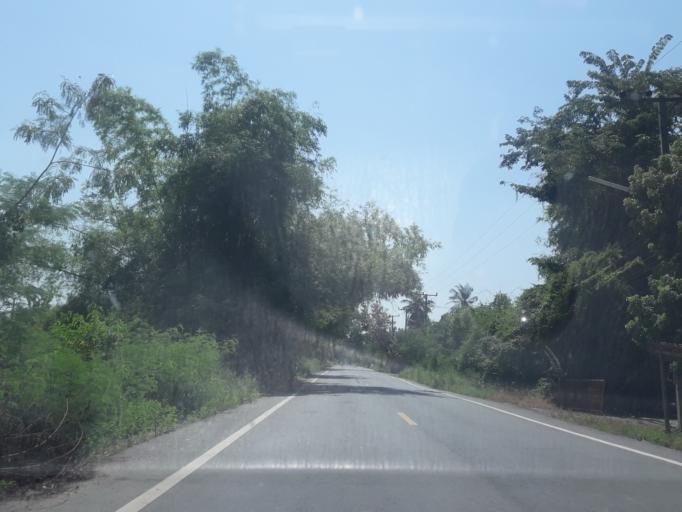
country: TH
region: Pathum Thani
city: Nong Suea
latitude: 14.1042
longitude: 100.8685
